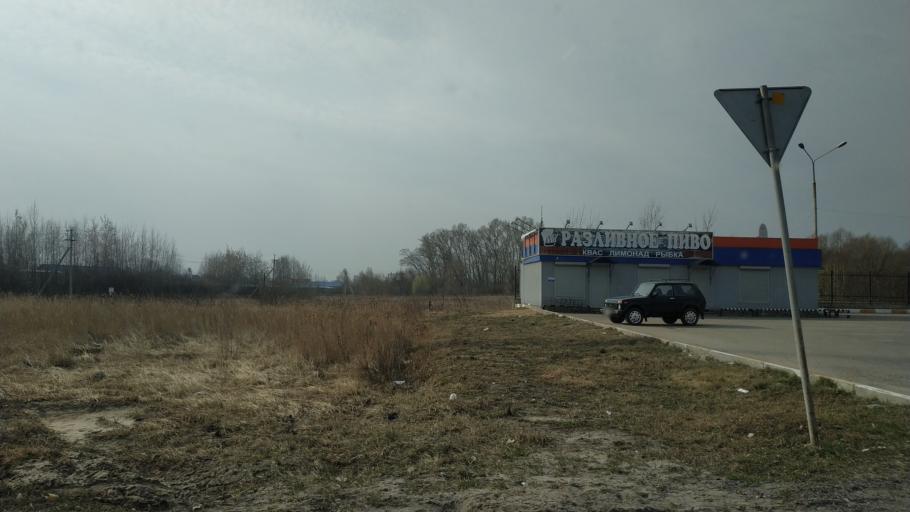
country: RU
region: Moskovskaya
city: Beloozerskiy
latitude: 55.4477
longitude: 38.4846
